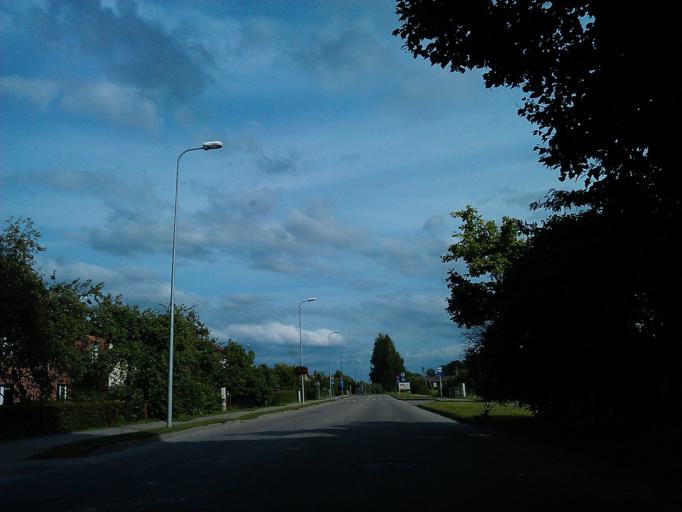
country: LV
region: Cesu Rajons
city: Cesis
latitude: 57.3040
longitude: 25.2904
